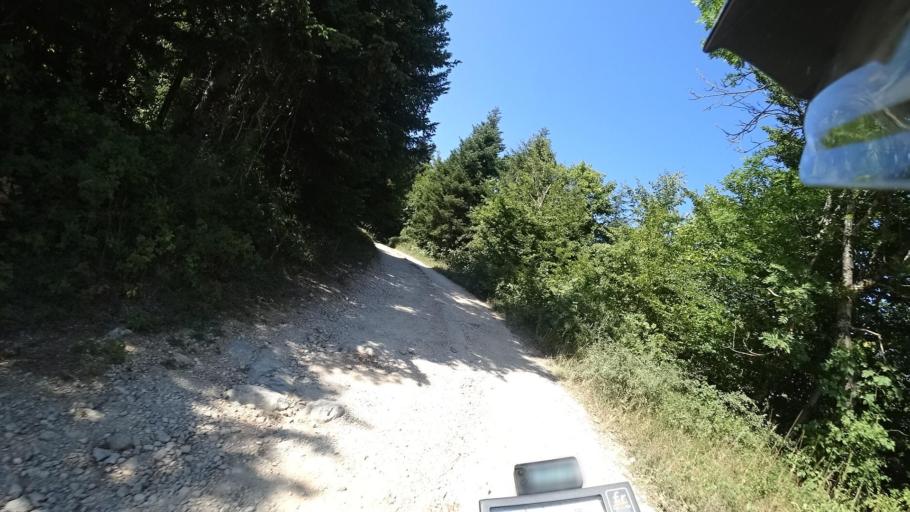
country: HR
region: Licko-Senjska
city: Otocac
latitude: 44.7945
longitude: 15.3997
